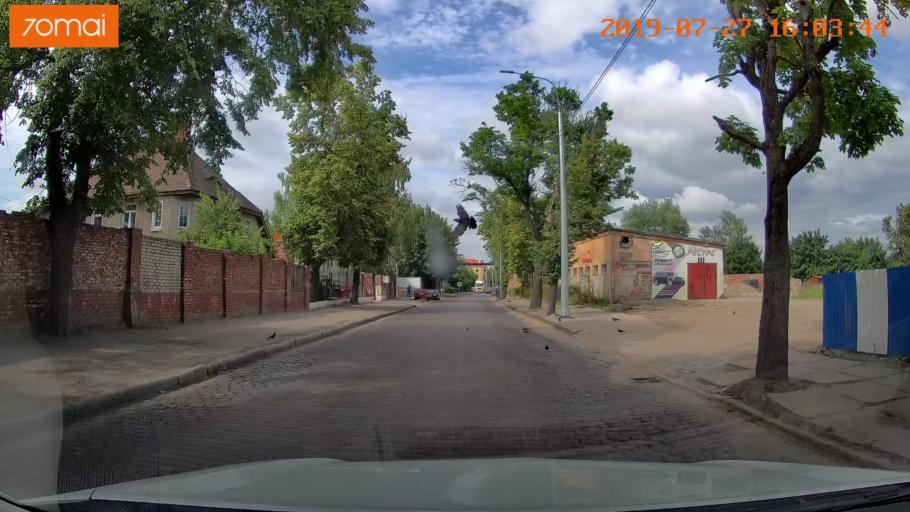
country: RU
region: Kaliningrad
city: Chernyakhovsk
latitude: 54.6335
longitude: 21.8031
